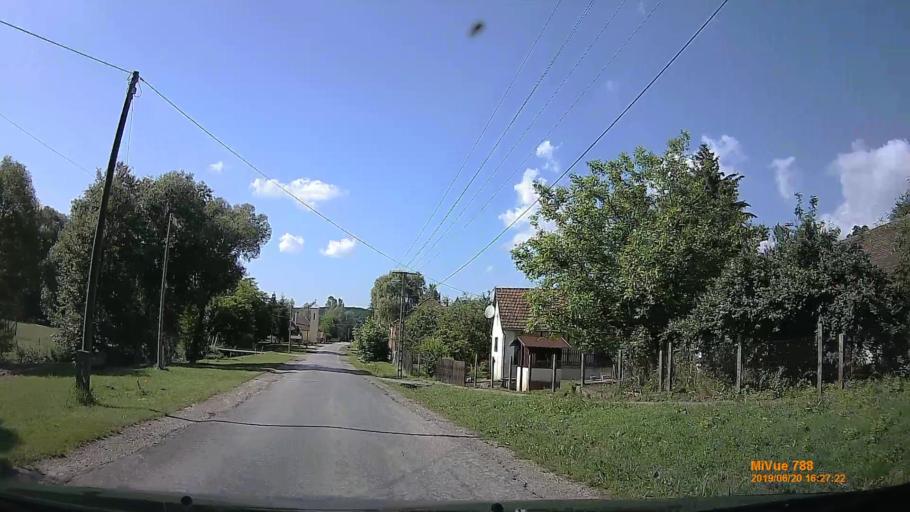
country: HU
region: Baranya
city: Buekkoesd
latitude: 46.1506
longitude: 18.0599
